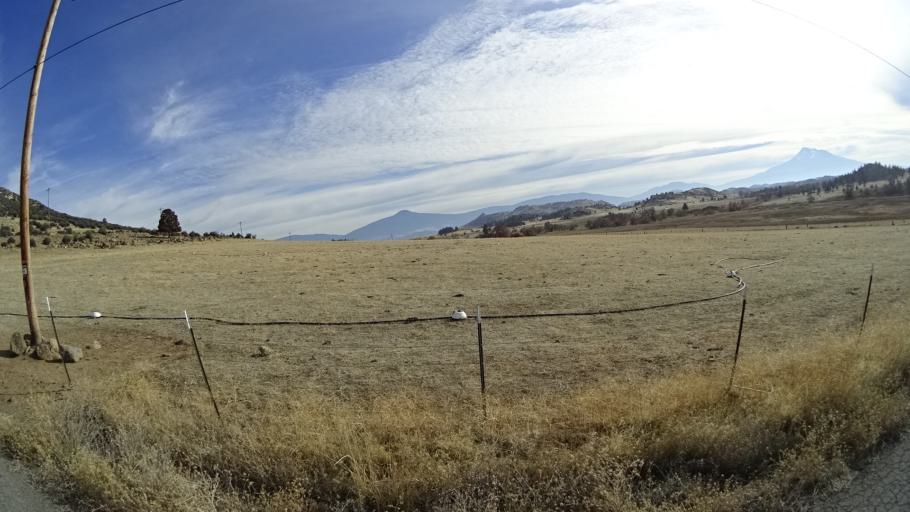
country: US
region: California
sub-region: Siskiyou County
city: Montague
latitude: 41.7066
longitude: -122.5154
